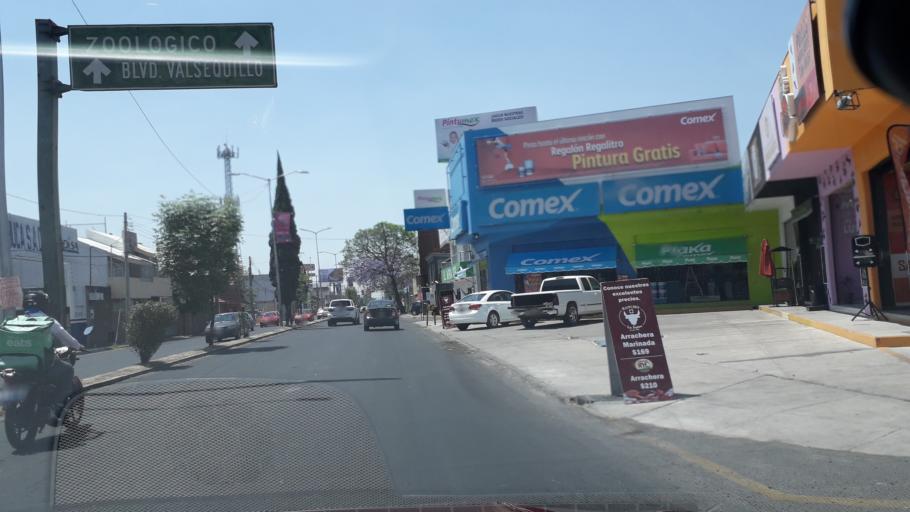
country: MX
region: Puebla
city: Puebla
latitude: 19.0228
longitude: -98.1919
